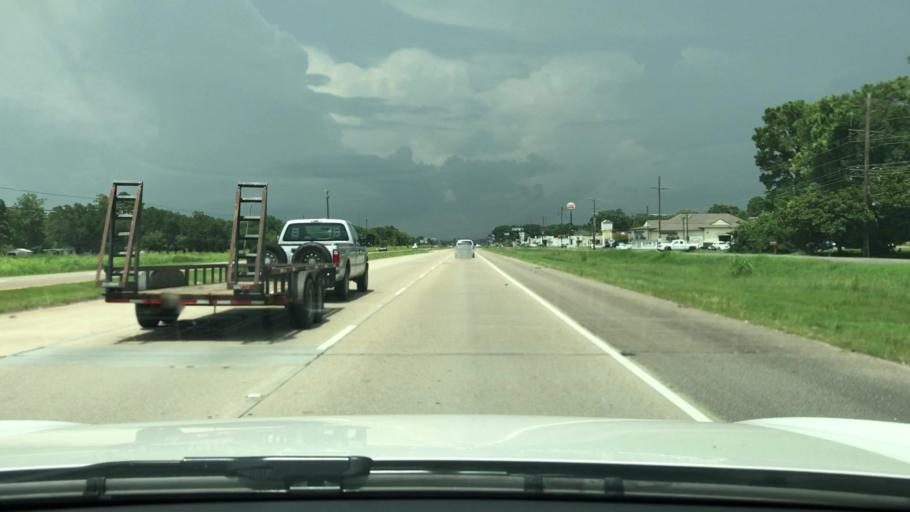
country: US
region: Louisiana
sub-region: West Baton Rouge Parish
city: Brusly
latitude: 30.4041
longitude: -91.2317
